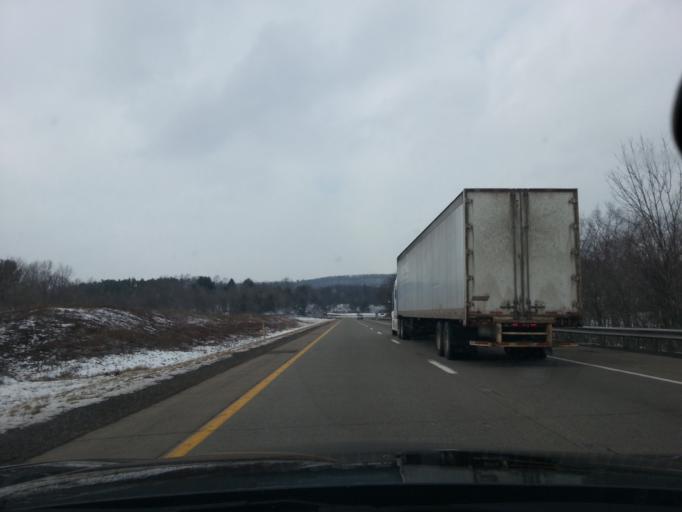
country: US
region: Pennsylvania
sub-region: Luzerne County
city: Conyngham
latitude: 41.0377
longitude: -76.0136
